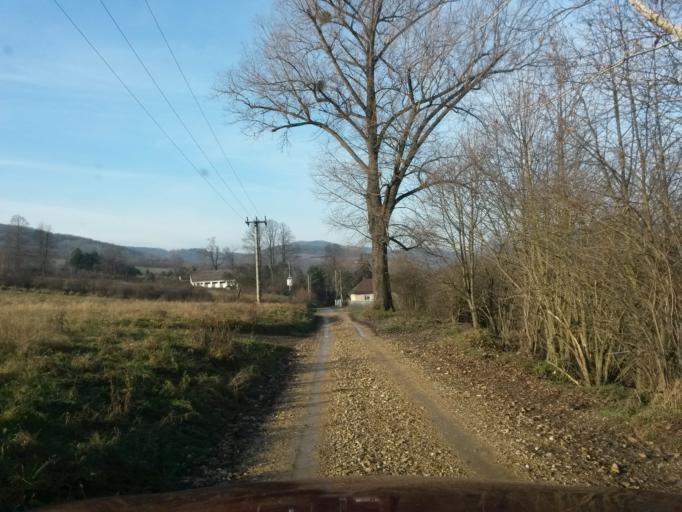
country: SK
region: Kosicky
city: Roznava
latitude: 48.7104
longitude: 20.4367
